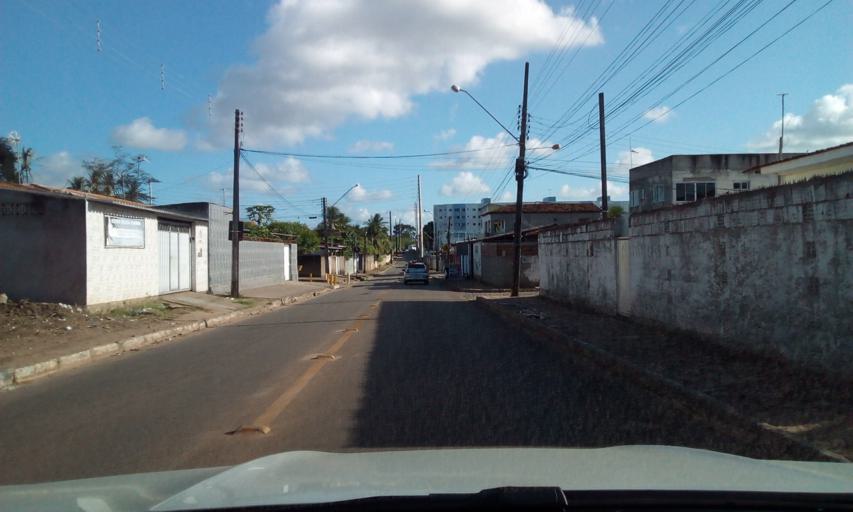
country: BR
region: Paraiba
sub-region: Bayeux
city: Bayeux
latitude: -7.1415
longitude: -34.9090
